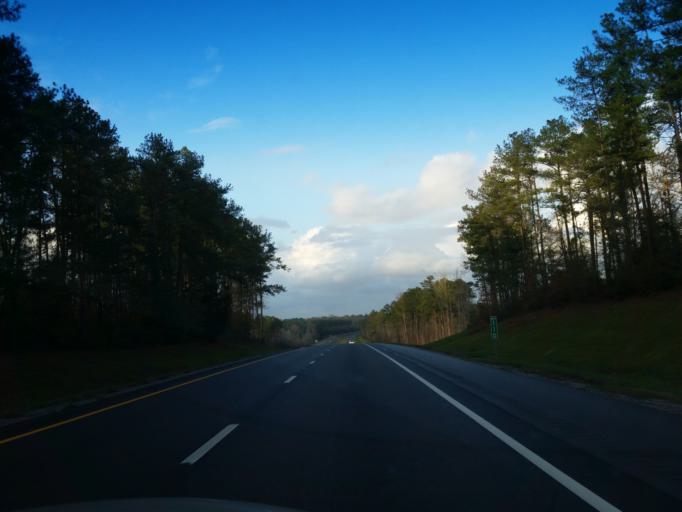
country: US
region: Mississippi
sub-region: Jones County
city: Sharon
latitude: 31.8603
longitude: -89.0469
